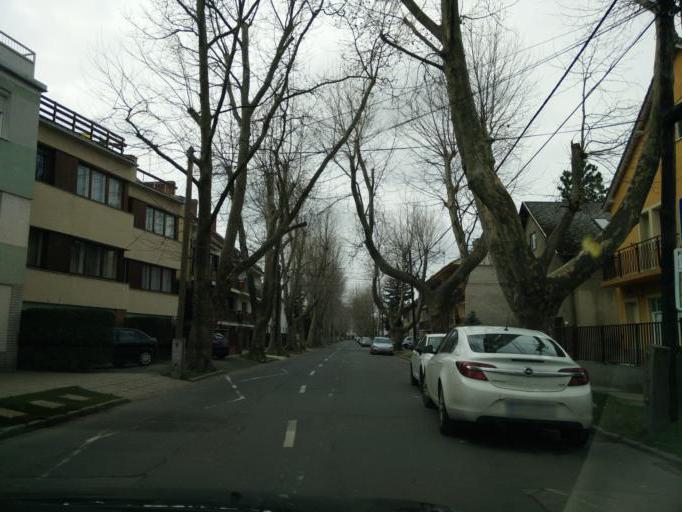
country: HU
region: Gyor-Moson-Sopron
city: Gyor
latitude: 47.6947
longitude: 17.6350
